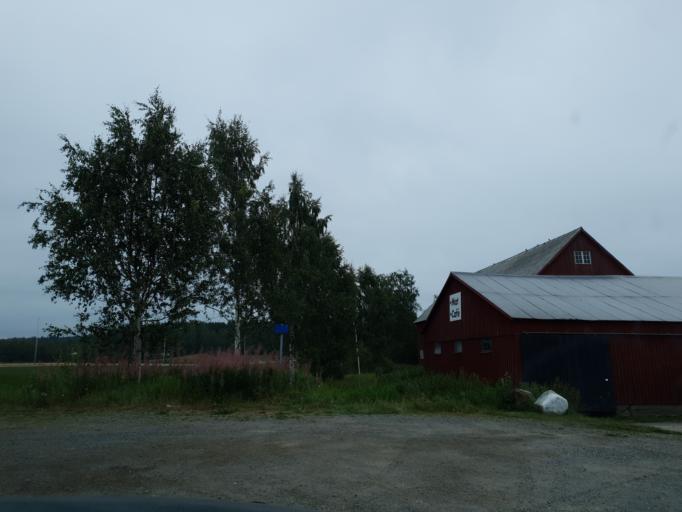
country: SE
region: Vaesterbotten
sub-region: Robertsfors Kommun
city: Robertsfors
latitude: 64.2726
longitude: 21.0512
